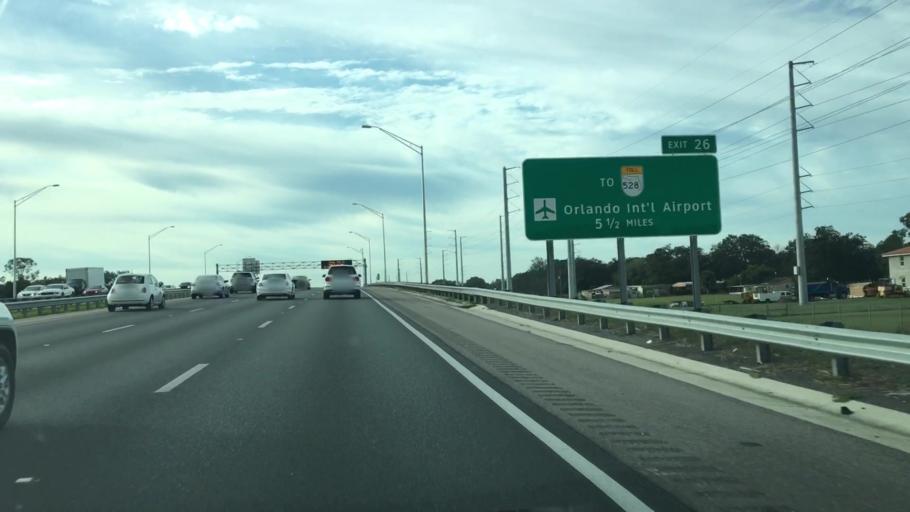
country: US
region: Florida
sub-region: Orange County
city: Azalea Park
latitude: 28.5273
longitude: -81.2510
